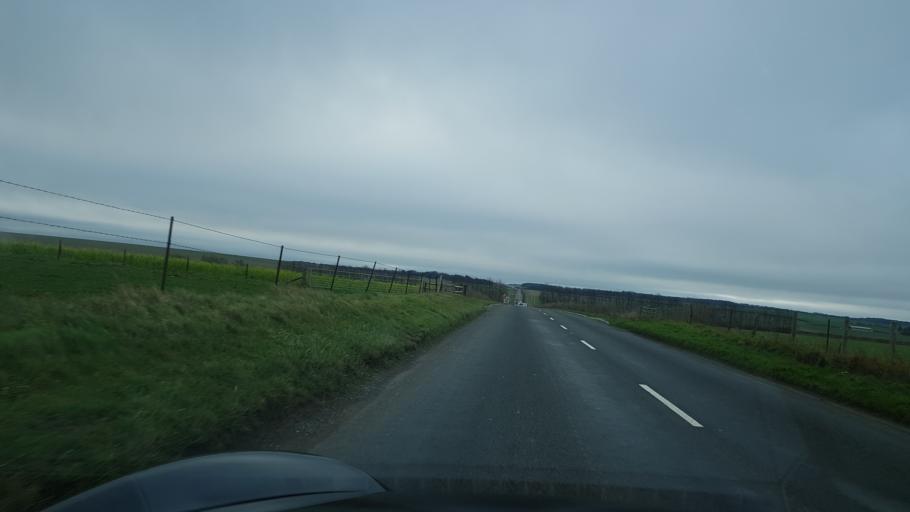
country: GB
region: England
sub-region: Wiltshire
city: Shrewton
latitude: 51.1889
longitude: -1.8610
